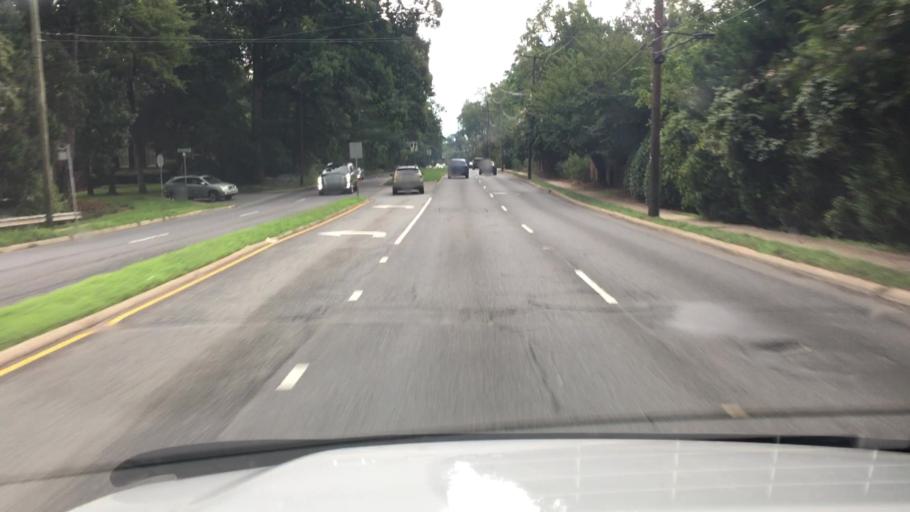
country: US
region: North Carolina
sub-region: Mecklenburg County
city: Charlotte
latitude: 35.1829
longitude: -80.8201
